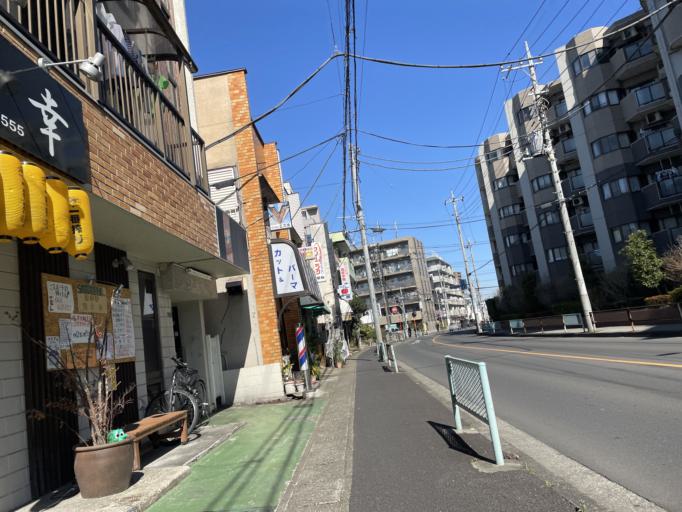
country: JP
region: Saitama
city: Shiki
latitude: 35.8118
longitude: 139.5808
